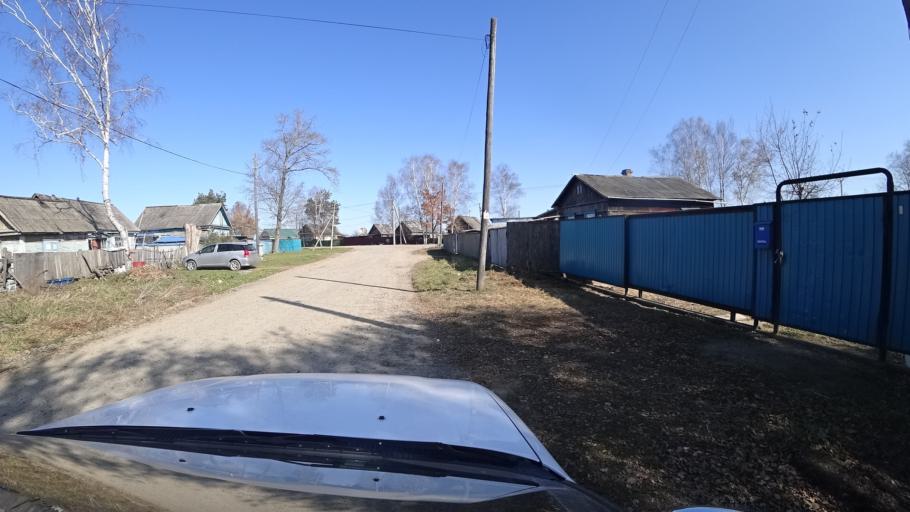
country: RU
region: Primorskiy
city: Dal'nerechensk
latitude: 45.9263
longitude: 133.7518
